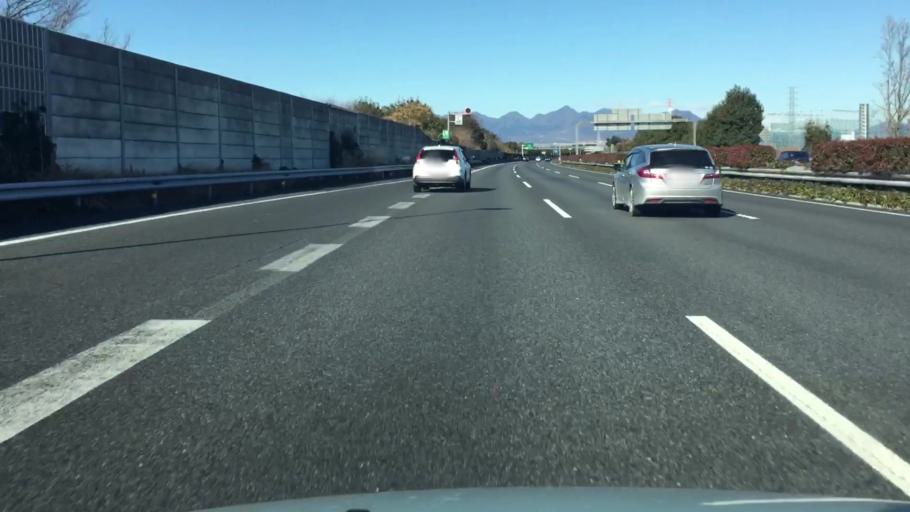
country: JP
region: Gunma
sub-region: Sawa-gun
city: Tamamura
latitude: 36.3245
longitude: 139.0700
